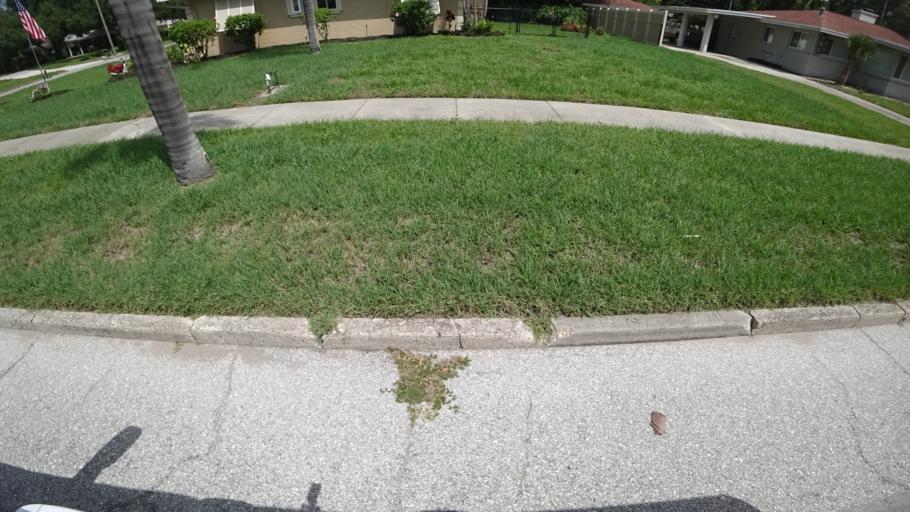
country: US
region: Florida
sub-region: Manatee County
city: Whitfield
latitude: 27.4100
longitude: -82.5747
